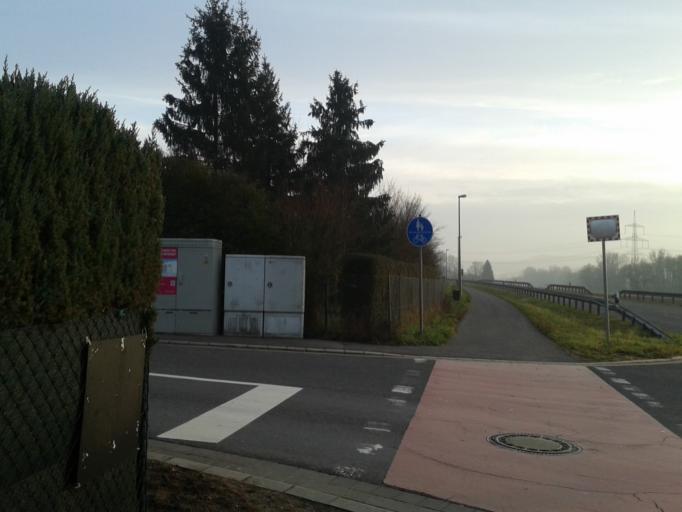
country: DE
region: Bavaria
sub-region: Upper Franconia
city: Gundelsheim
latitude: 49.9392
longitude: 10.9299
